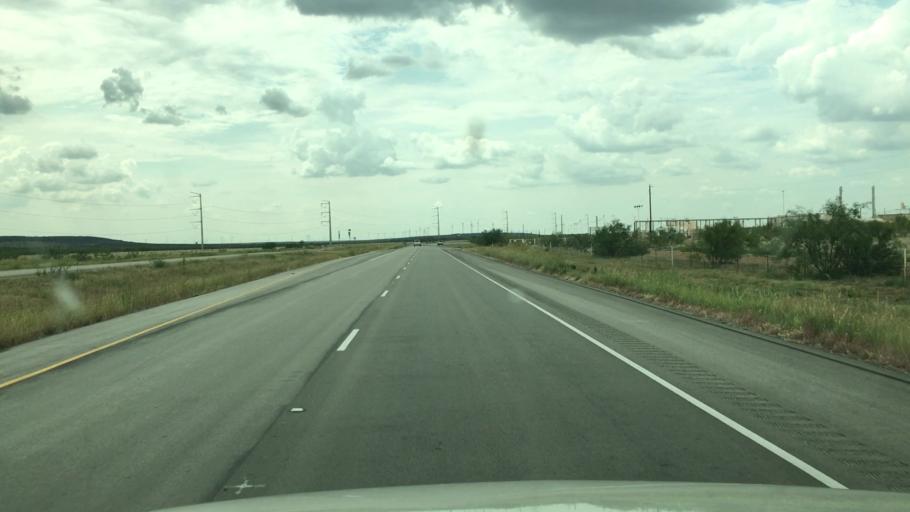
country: US
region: Texas
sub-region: Glasscock County
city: Garden City
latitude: 31.9673
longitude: -101.2342
